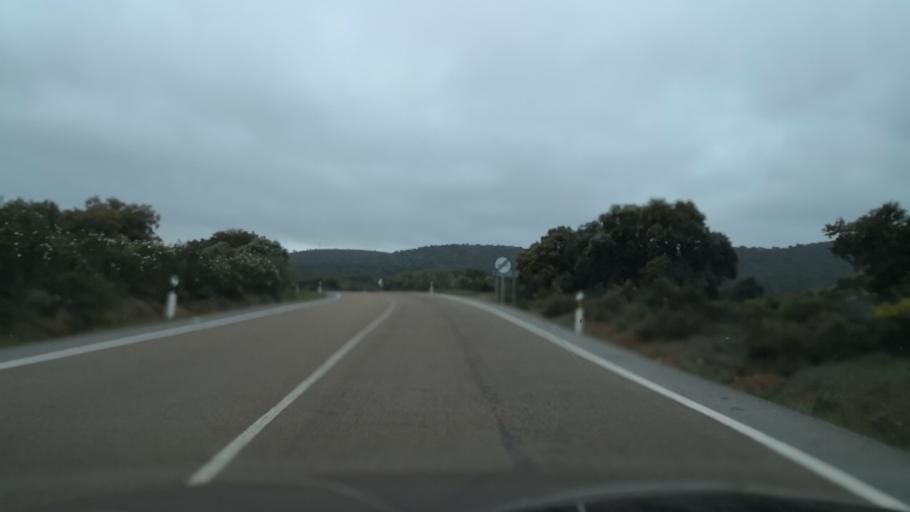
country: ES
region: Extremadura
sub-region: Provincia de Badajoz
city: Puebla de Obando
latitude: 39.2912
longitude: -6.5222
